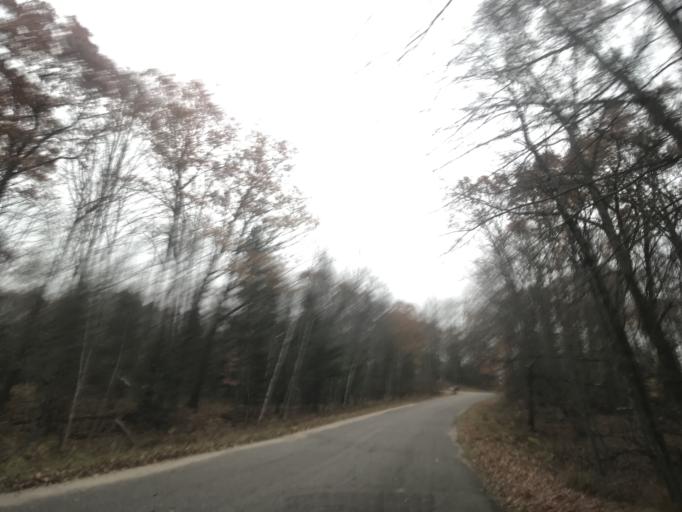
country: US
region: Michigan
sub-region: Dickinson County
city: Kingsford
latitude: 45.3785
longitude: -88.3216
